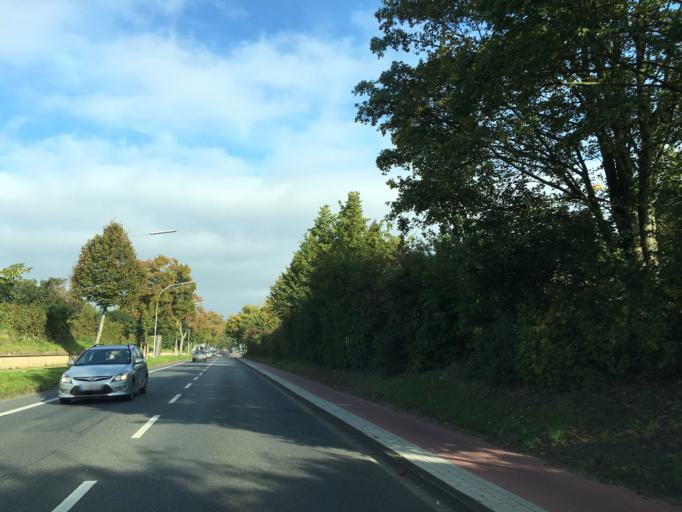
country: DE
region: Lower Saxony
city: Lueneburg
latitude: 53.2638
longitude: 10.4073
